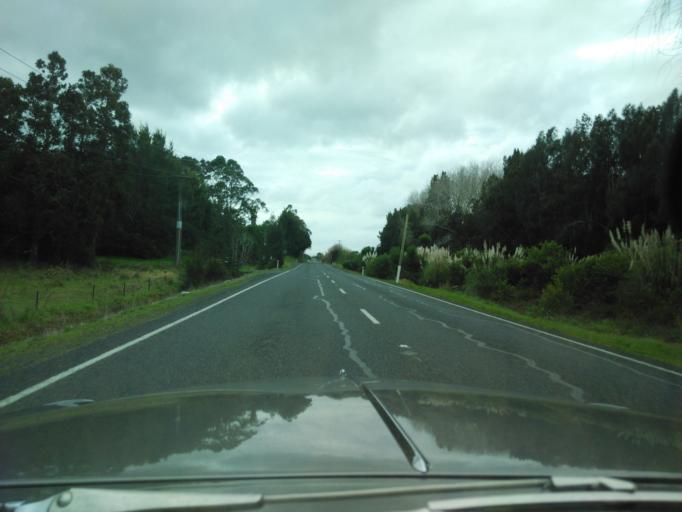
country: NZ
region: Auckland
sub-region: Auckland
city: Muriwai Beach
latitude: -36.7337
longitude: 174.4410
